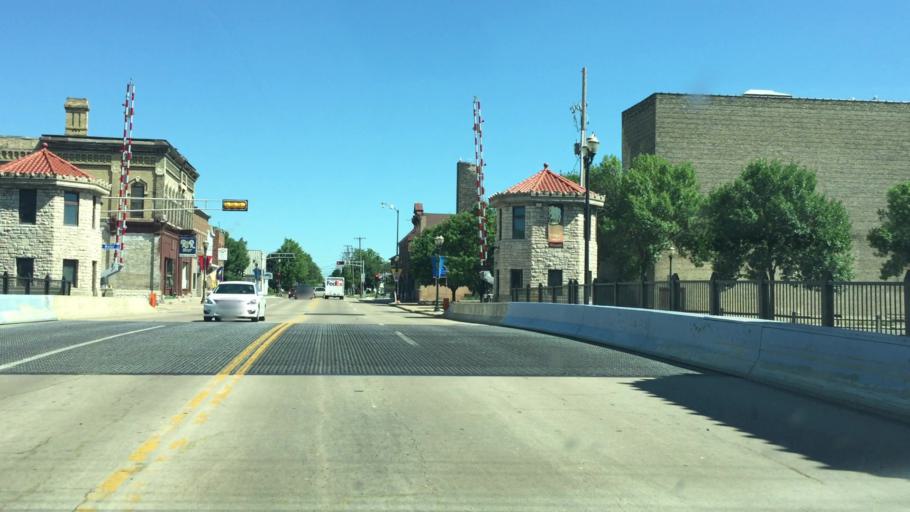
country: US
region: Wisconsin
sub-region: Winnebago County
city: Menasha
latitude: 44.1981
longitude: -88.4532
